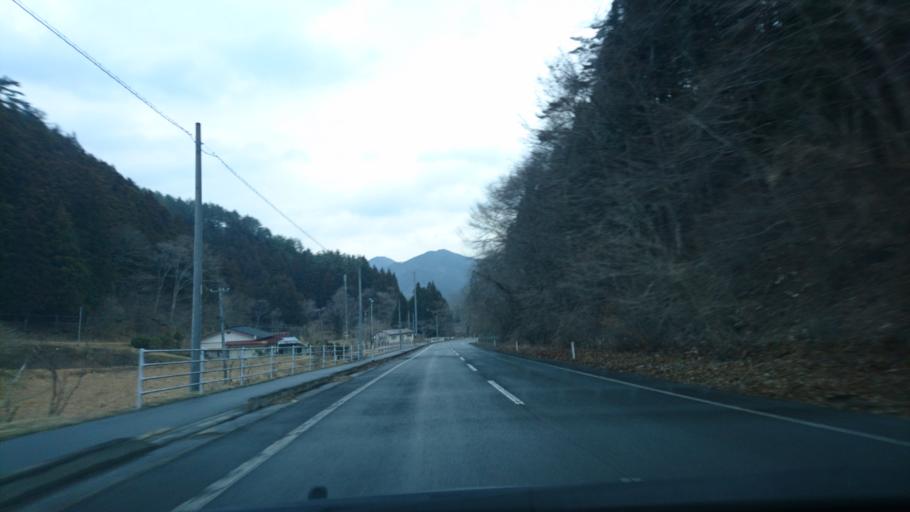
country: JP
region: Iwate
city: Ofunato
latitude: 39.0094
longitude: 141.5447
